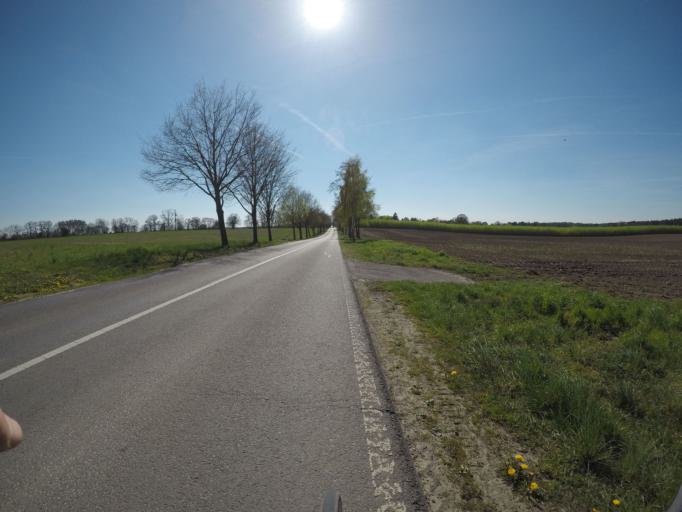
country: DE
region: Brandenburg
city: Rehfelde
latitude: 52.5581
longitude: 13.9550
